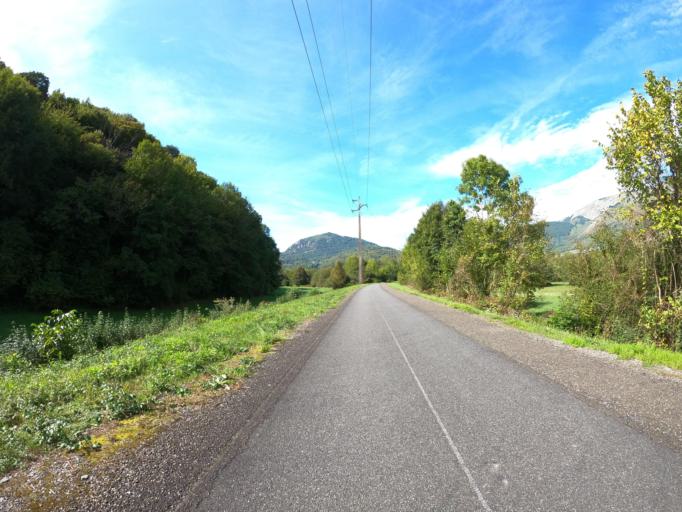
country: FR
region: Midi-Pyrenees
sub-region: Departement des Hautes-Pyrenees
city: Argeles-Gazost
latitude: 43.0225
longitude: -0.0794
